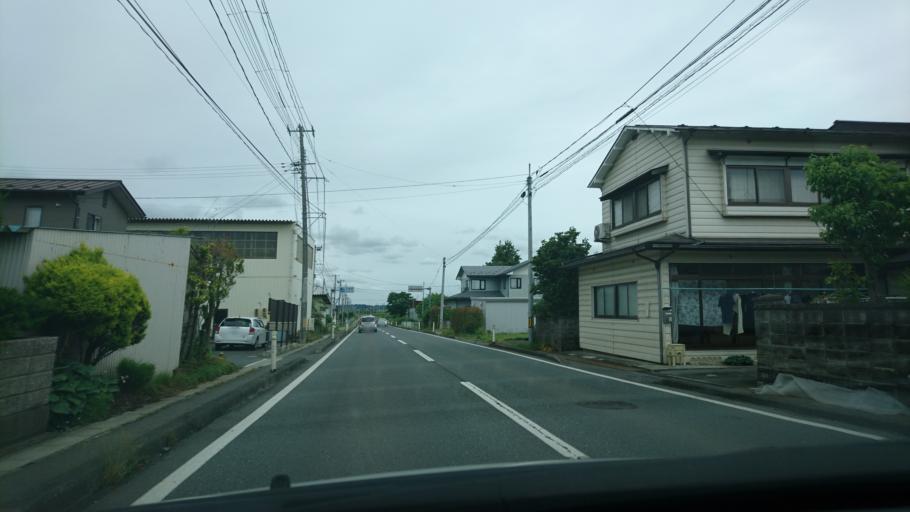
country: JP
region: Iwate
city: Ichinoseki
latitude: 38.9573
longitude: 141.1292
